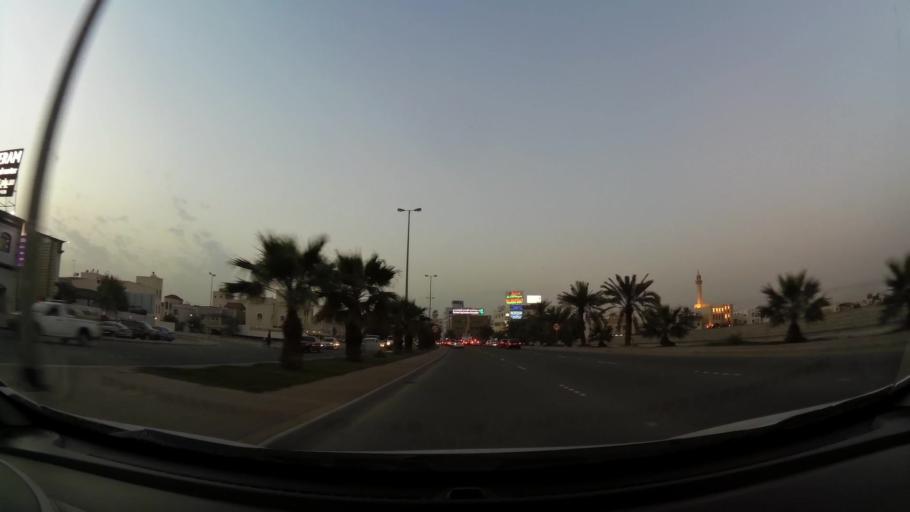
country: BH
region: Manama
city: Manama
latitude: 26.2066
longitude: 50.5674
